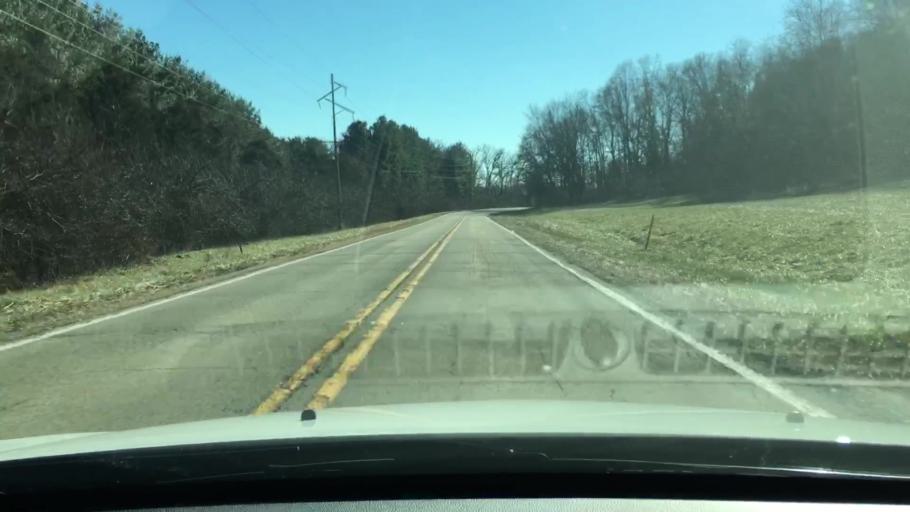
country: US
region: Illinois
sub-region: Fulton County
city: Astoria
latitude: 40.2045
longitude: -90.2031
